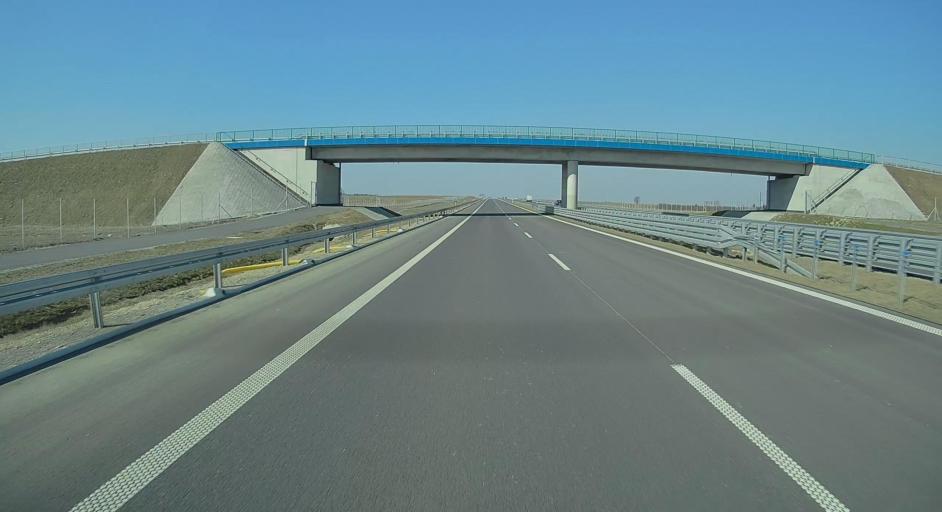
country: PL
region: Lublin Voivodeship
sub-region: Powiat janowski
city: Modliborzyce
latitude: 50.7410
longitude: 22.3177
